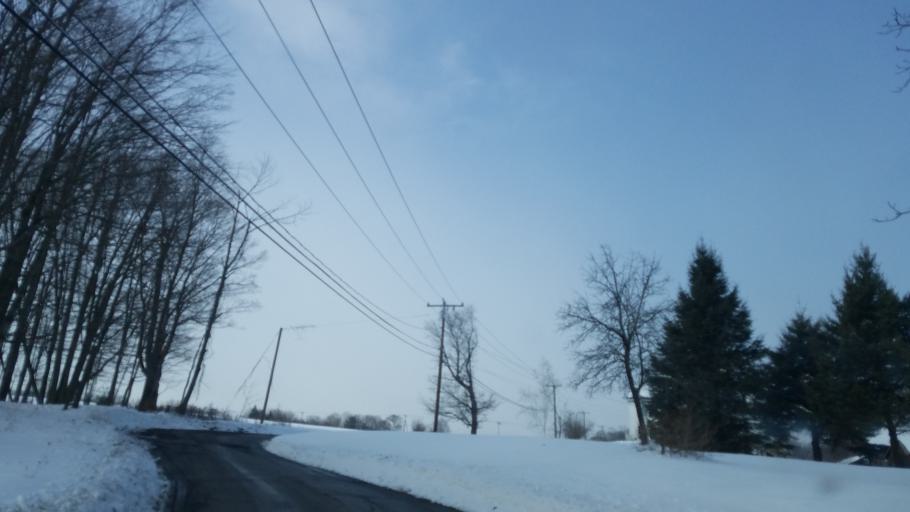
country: US
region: Connecticut
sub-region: Hartford County
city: Canton Valley
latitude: 41.8469
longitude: -72.9019
